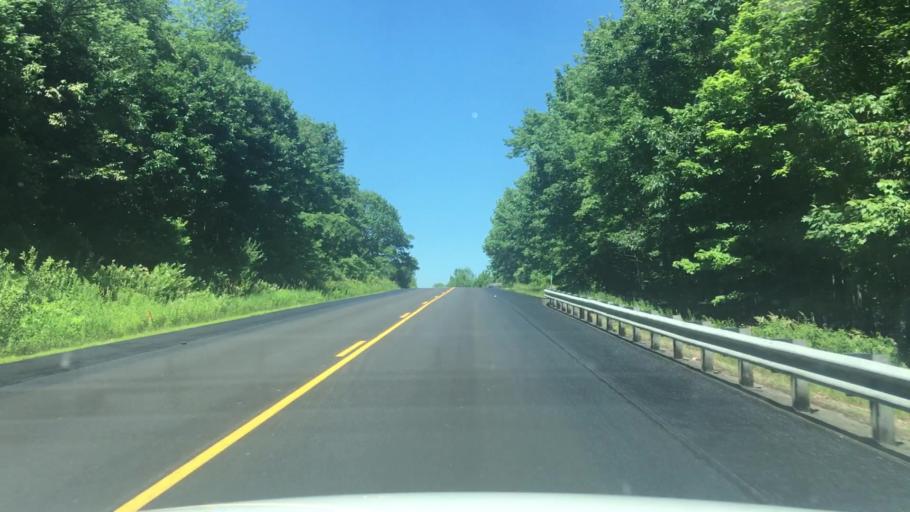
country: US
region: Maine
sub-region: Waldo County
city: Searsmont
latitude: 44.4061
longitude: -69.3028
